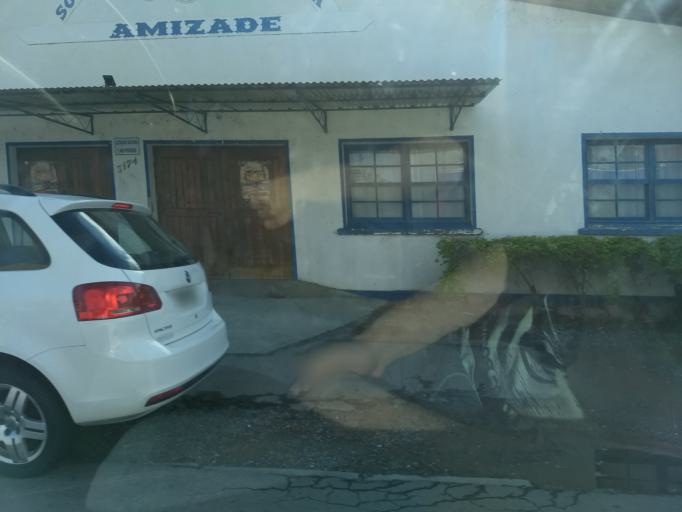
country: BR
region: Santa Catarina
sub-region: Jaragua Do Sul
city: Jaragua do Sul
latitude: -26.4528
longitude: -49.1076
